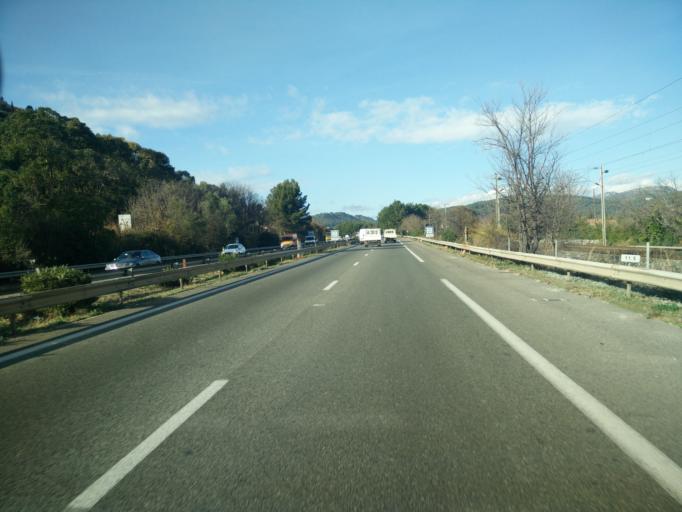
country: FR
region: Provence-Alpes-Cote d'Azur
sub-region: Departement du Var
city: Sollies-Ville
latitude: 43.1806
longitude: 6.0459
